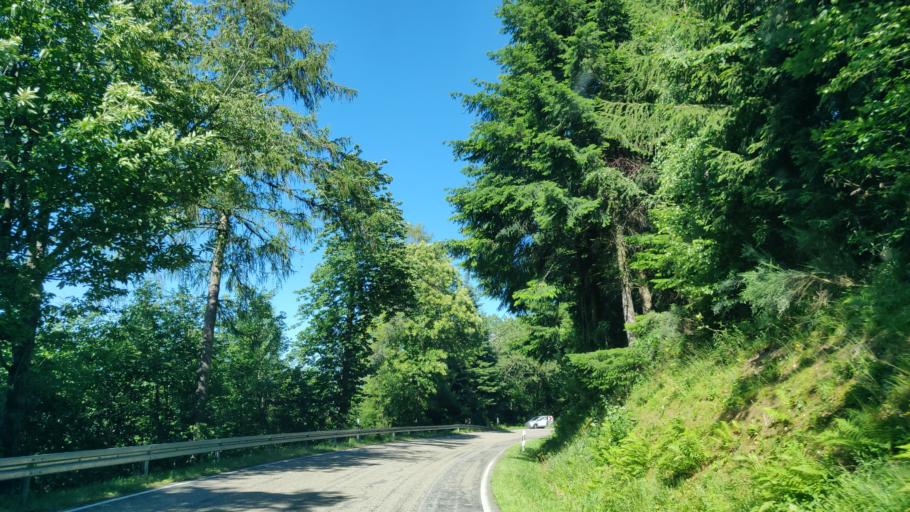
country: DE
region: Baden-Wuerttemberg
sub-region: Karlsruhe Region
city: Gernsbach
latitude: 48.7513
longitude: 8.3168
